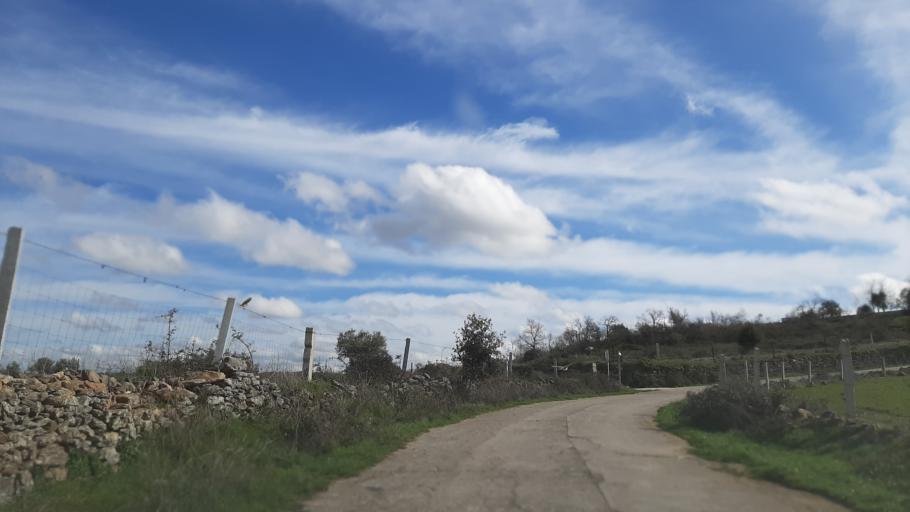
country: ES
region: Castille and Leon
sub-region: Provincia de Salamanca
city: Villarino de los Aires
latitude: 41.2531
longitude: -6.5236
